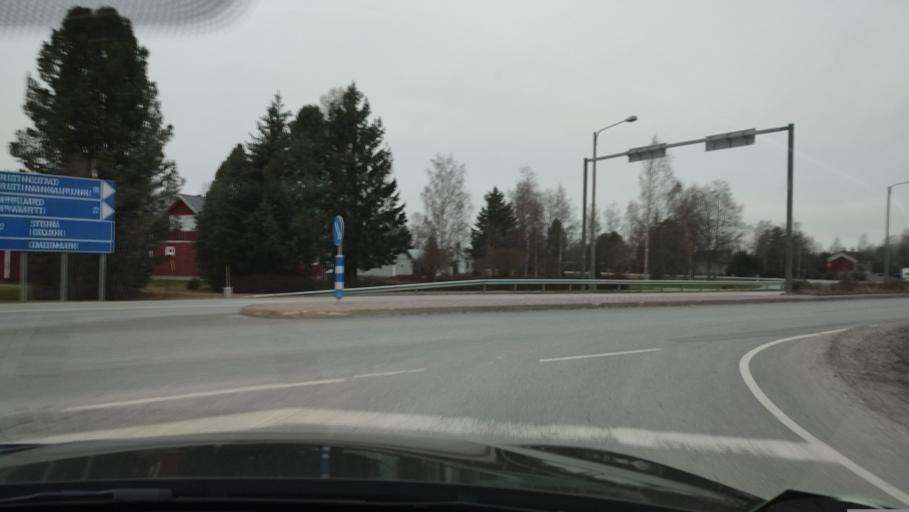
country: FI
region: Ostrobothnia
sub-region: Sydosterbotten
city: Kristinestad
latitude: 62.2612
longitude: 21.5337
